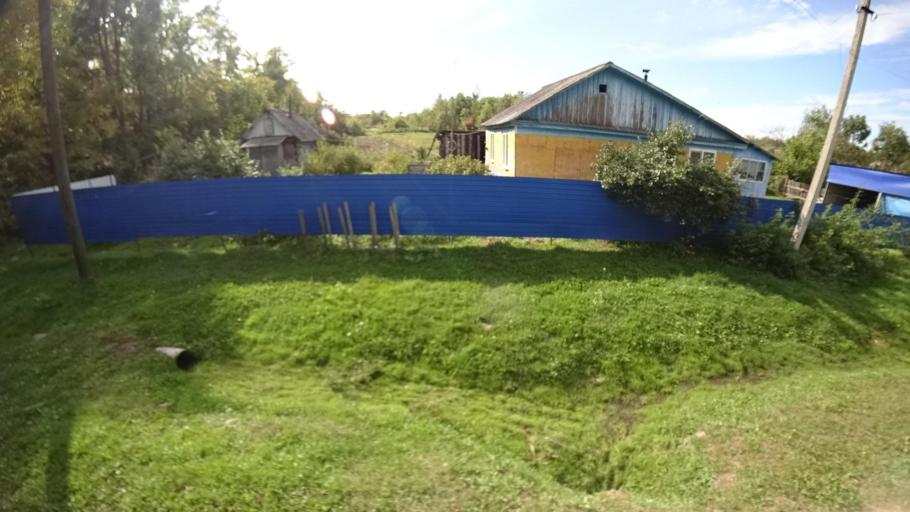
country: RU
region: Primorskiy
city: Dostoyevka
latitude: 44.2946
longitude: 133.4590
